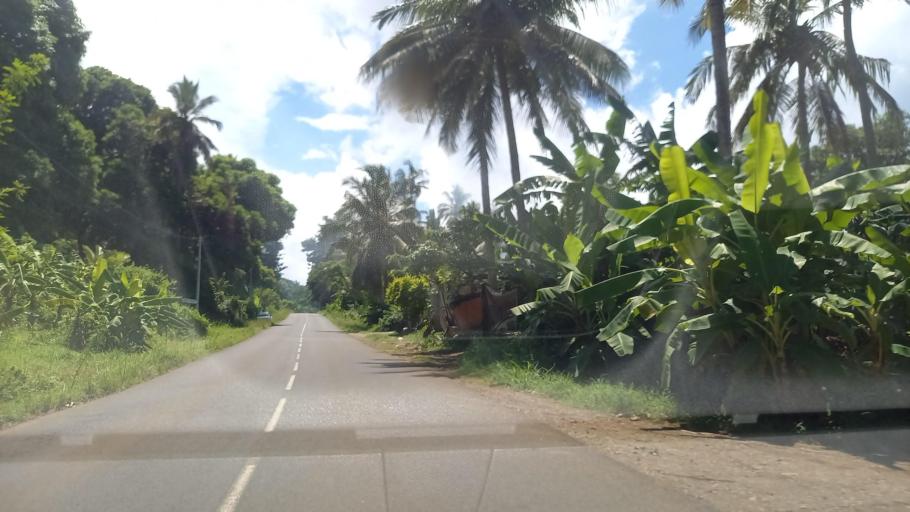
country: YT
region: Sada
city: Sada
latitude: -12.8733
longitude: 45.1192
